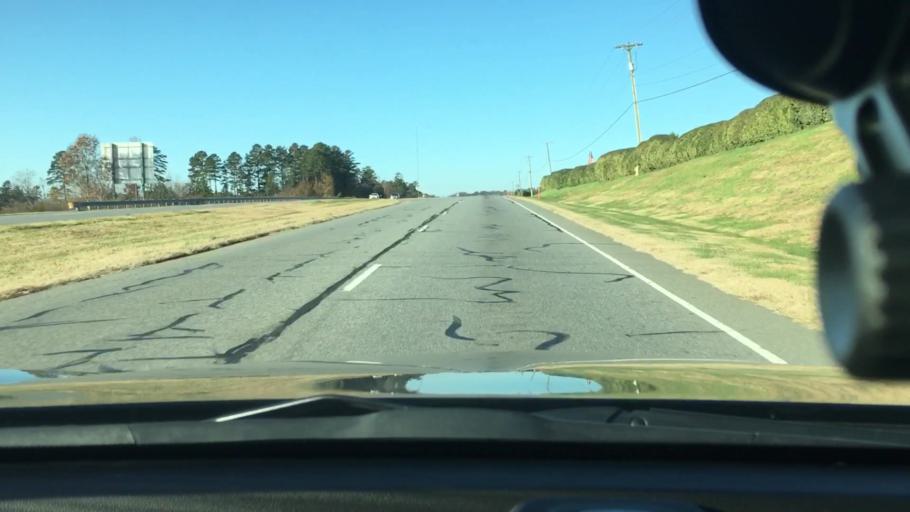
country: US
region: North Carolina
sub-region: Cabarrus County
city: Concord
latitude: 35.3700
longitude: -80.5677
